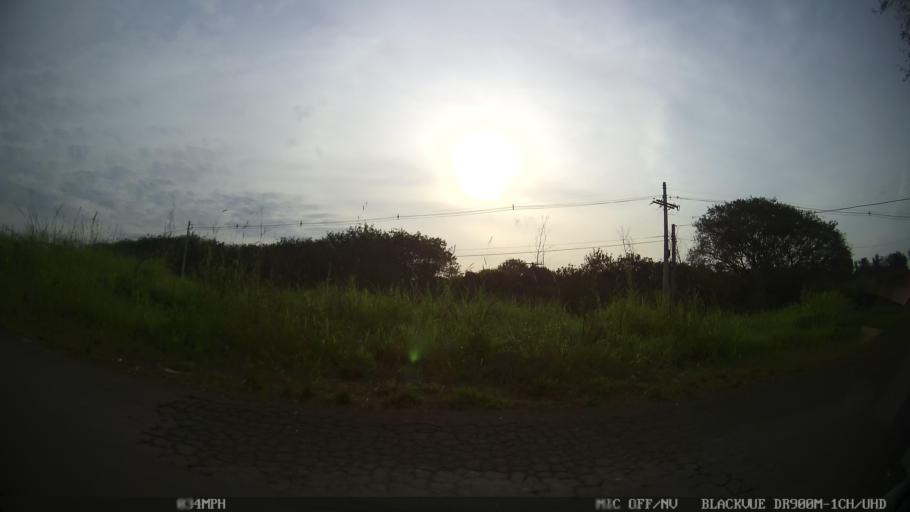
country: BR
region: Sao Paulo
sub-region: Piracicaba
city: Piracicaba
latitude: -22.6979
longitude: -47.5881
